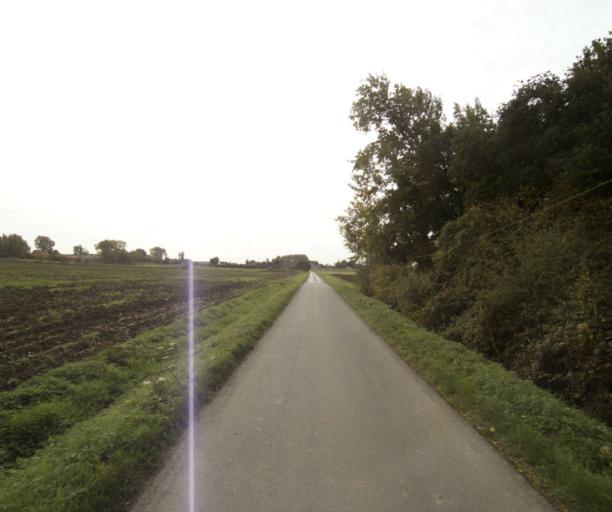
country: FR
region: Nord-Pas-de-Calais
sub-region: Departement du Nord
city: Fournes-en-Weppes
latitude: 50.6129
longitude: 2.8640
